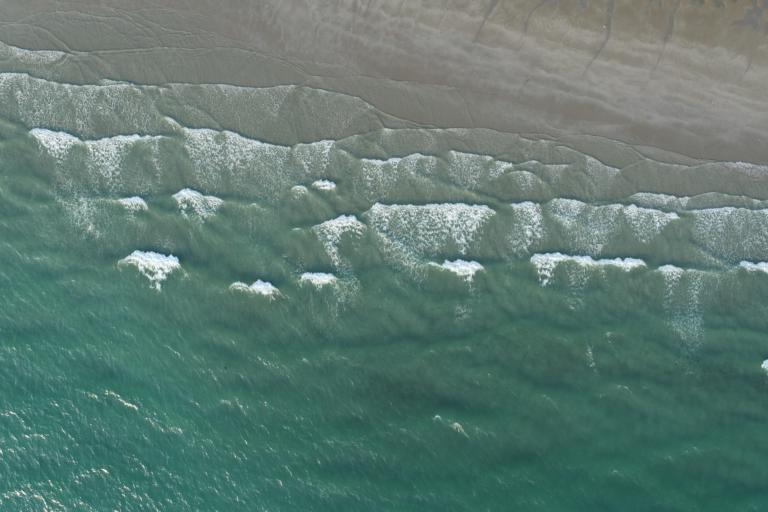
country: TH
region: Rayong
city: Rayong
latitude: 12.5977
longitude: 101.4065
